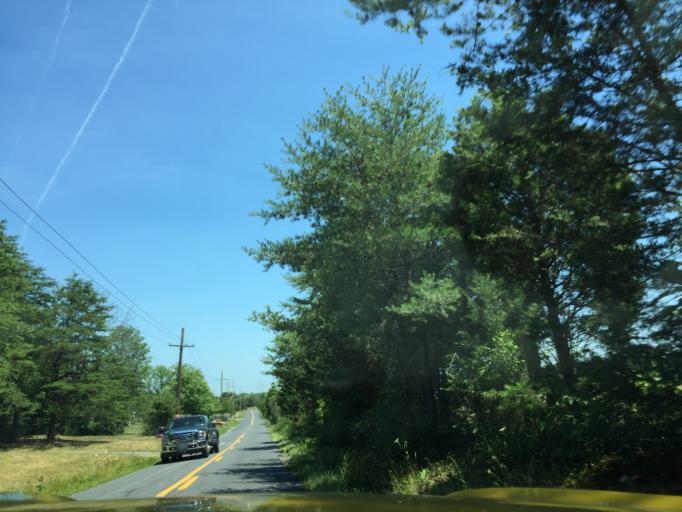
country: US
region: West Virginia
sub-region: Berkeley County
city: Inwood
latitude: 39.3265
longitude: -78.0178
